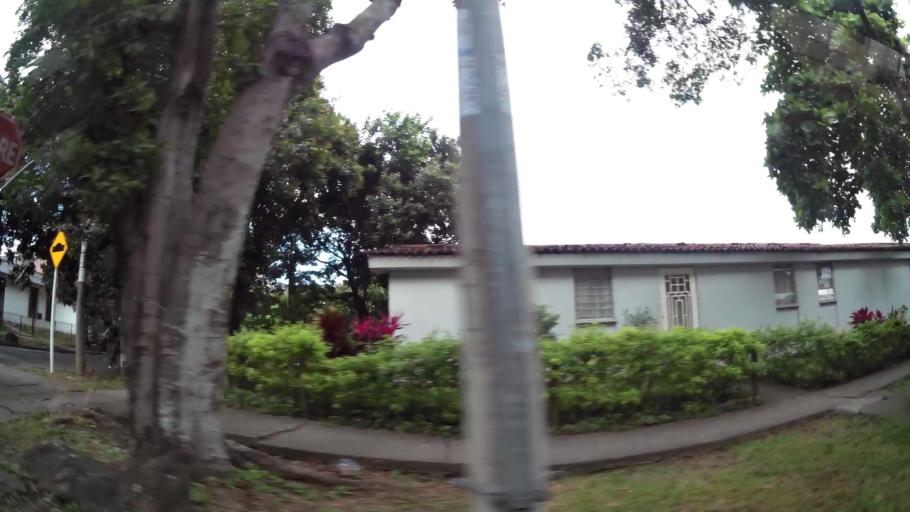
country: CO
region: Valle del Cauca
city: Cali
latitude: 3.4824
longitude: -76.5195
